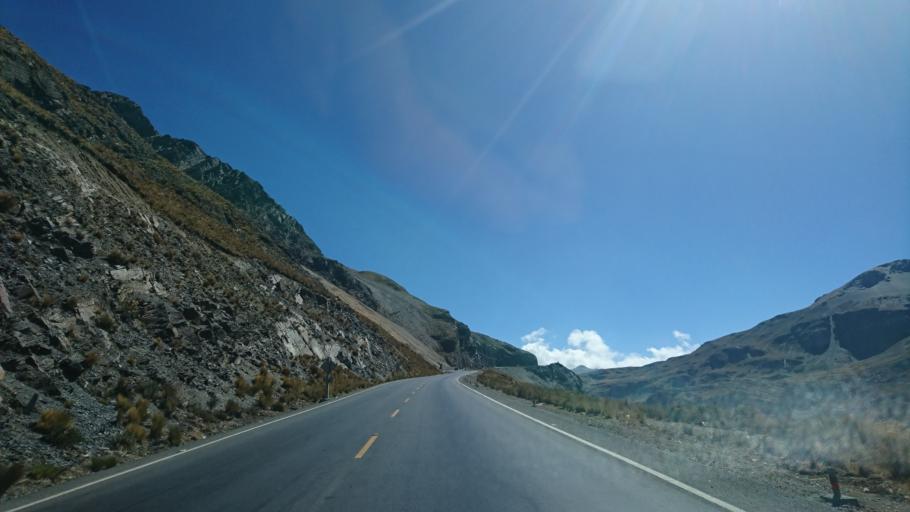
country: BO
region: La Paz
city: La Paz
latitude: -16.3917
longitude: -68.0438
